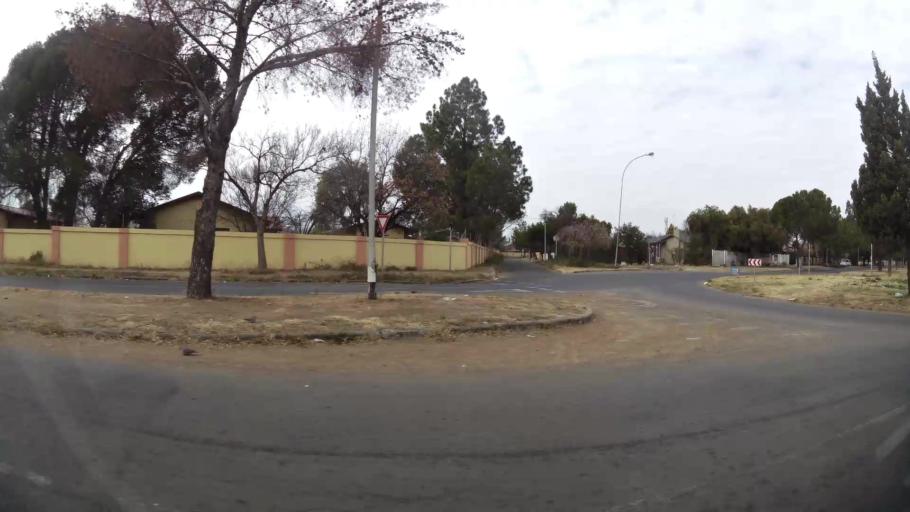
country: ZA
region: Orange Free State
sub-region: Mangaung Metropolitan Municipality
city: Bloemfontein
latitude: -29.1271
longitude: 26.2021
